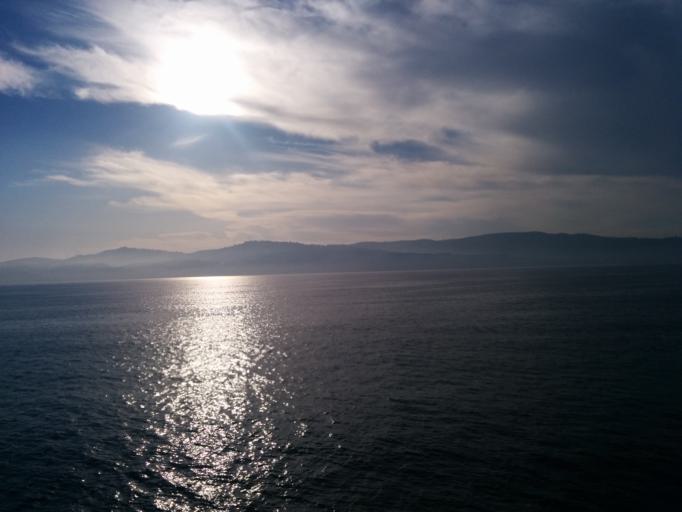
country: MA
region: Tanger-Tetouan
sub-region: Tanger-Assilah
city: Tangier
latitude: 35.8061
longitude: -5.7836
